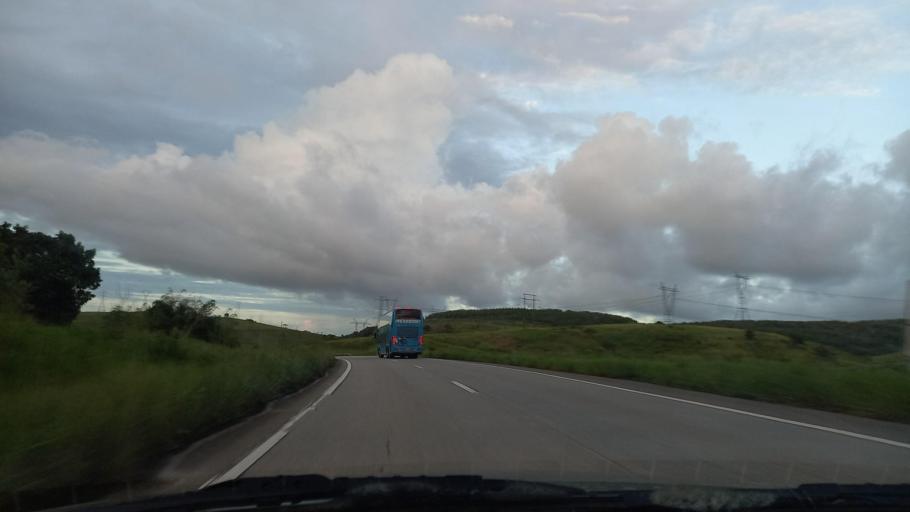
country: BR
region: Pernambuco
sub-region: Joaquim Nabuco
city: Joaquim Nabuco
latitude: -8.6032
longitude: -35.5340
